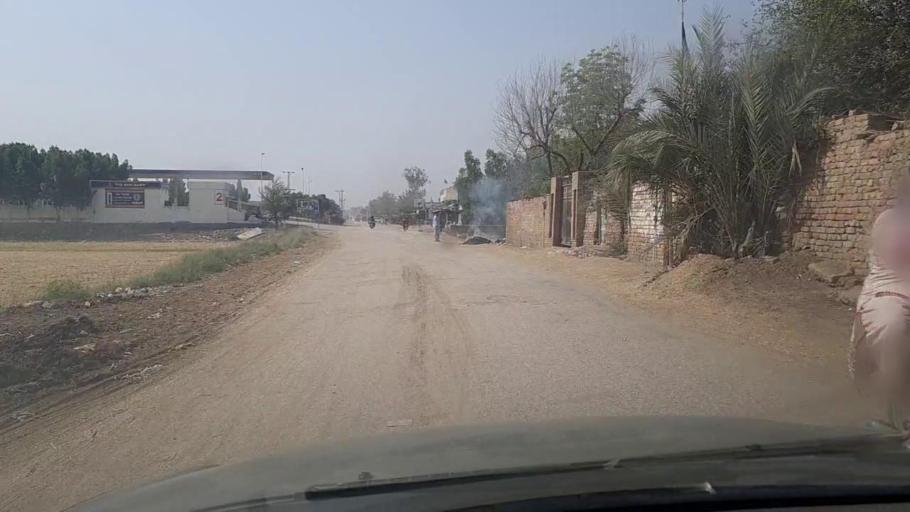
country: PK
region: Sindh
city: Mirpur Mathelo
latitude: 28.0146
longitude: 69.5474
